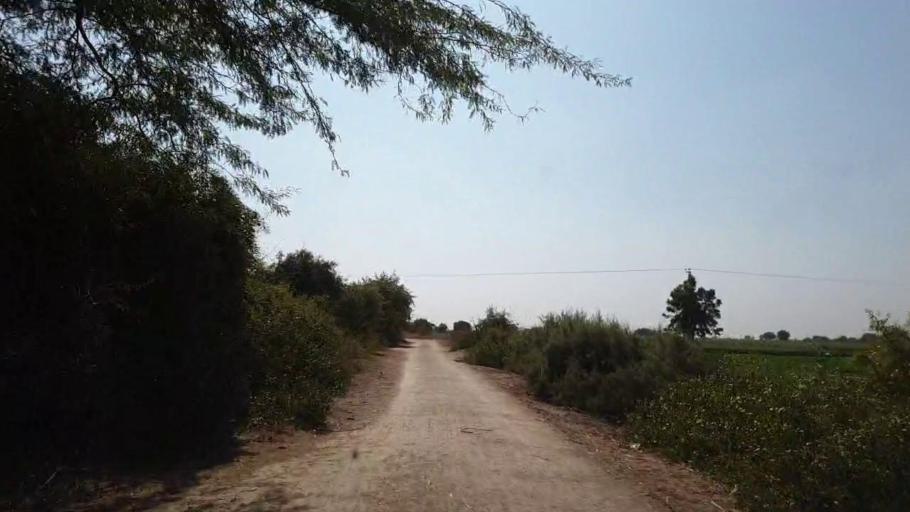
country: PK
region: Sindh
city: Mirpur Khas
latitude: 25.7272
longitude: 69.0705
